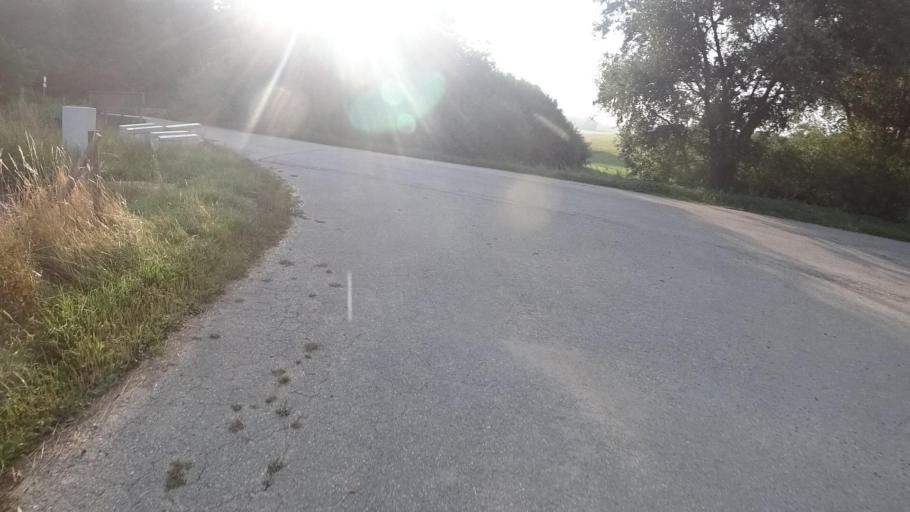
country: DE
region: Rheinland-Pfalz
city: Holzbach
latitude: 49.9551
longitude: 7.5220
